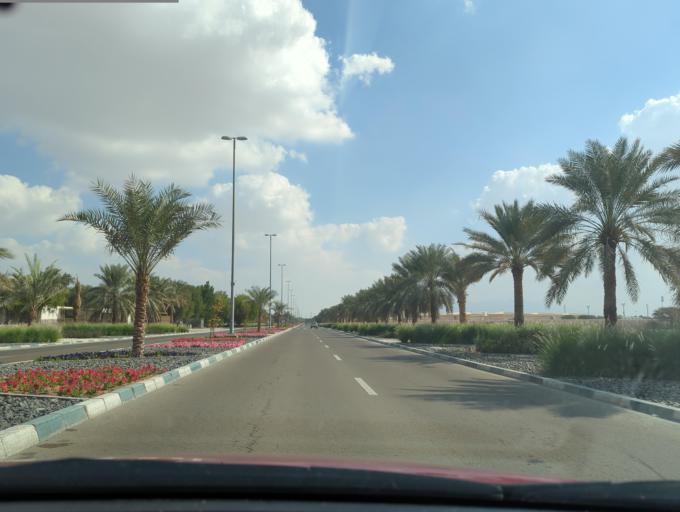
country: AE
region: Abu Dhabi
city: Al Ain
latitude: 24.1846
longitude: 55.6389
